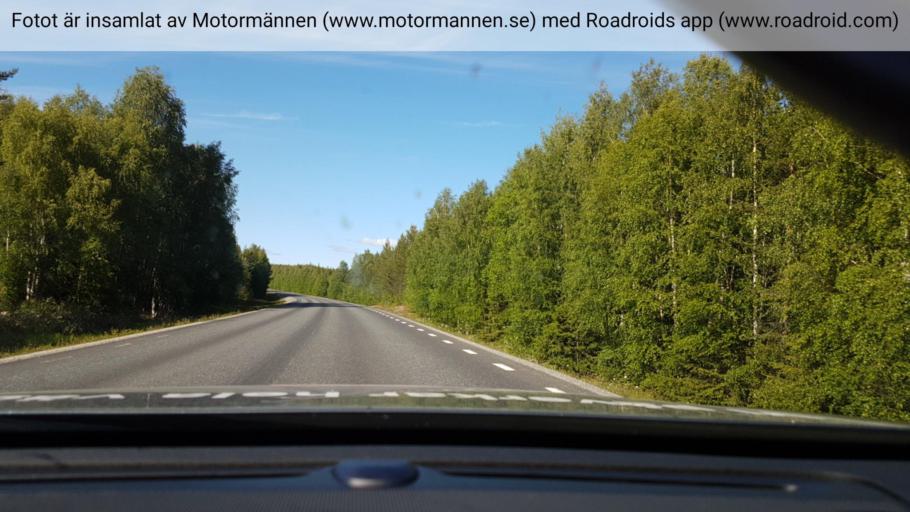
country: SE
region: Vaesterbotten
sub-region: Lycksele Kommun
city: Lycksele
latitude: 64.7783
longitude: 18.7337
